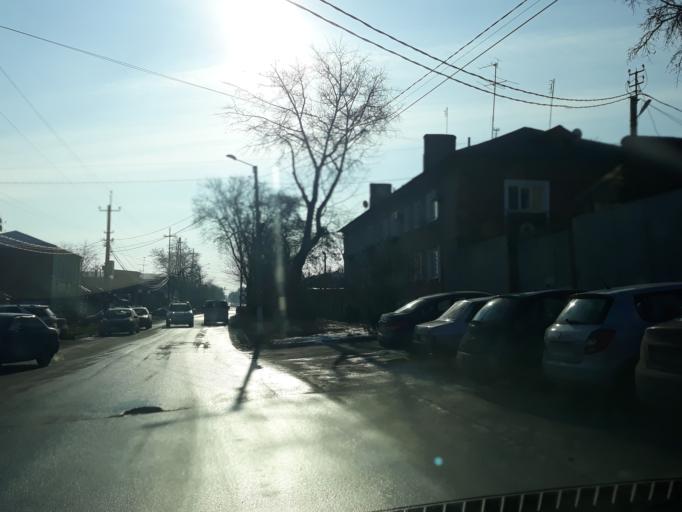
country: RU
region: Rostov
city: Taganrog
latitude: 47.2228
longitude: 38.9137
